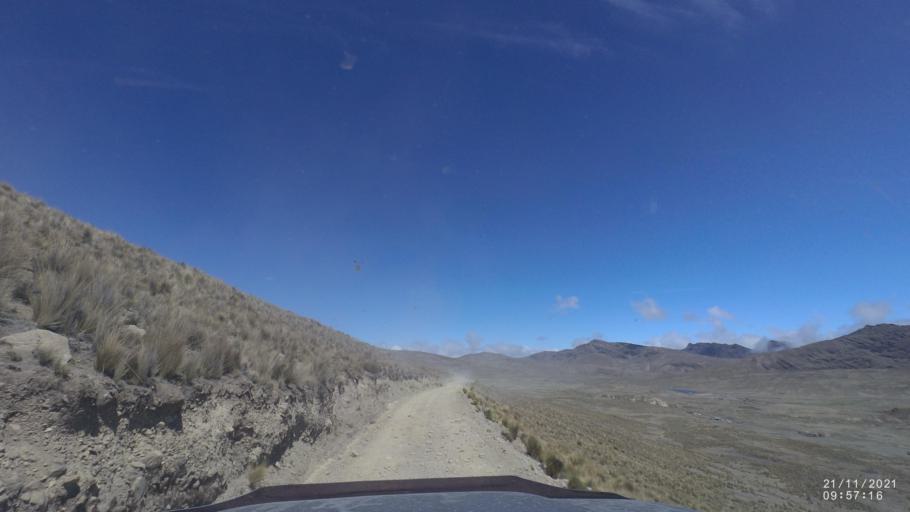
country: BO
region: Cochabamba
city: Cochabamba
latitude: -17.0397
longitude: -66.2703
